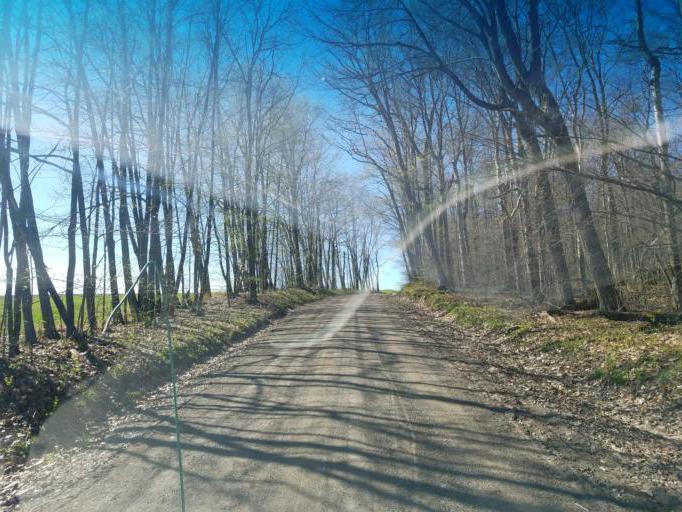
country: US
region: New York
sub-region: Allegany County
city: Andover
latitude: 41.9785
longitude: -77.7862
